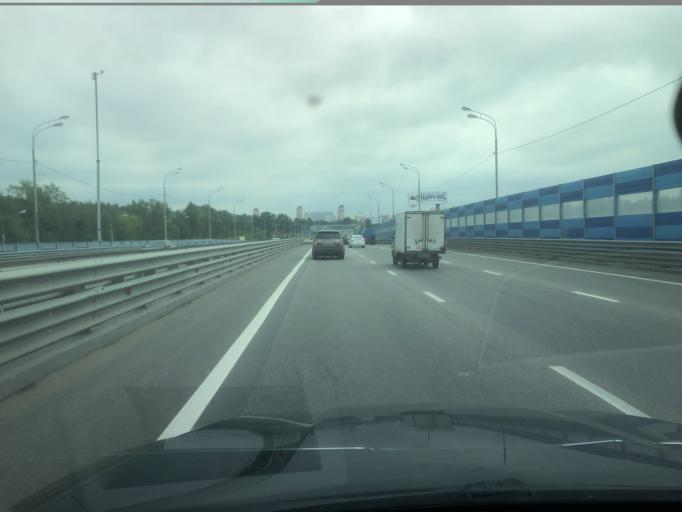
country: RU
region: Moscow
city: Severnyy
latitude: 55.9493
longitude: 37.5396
